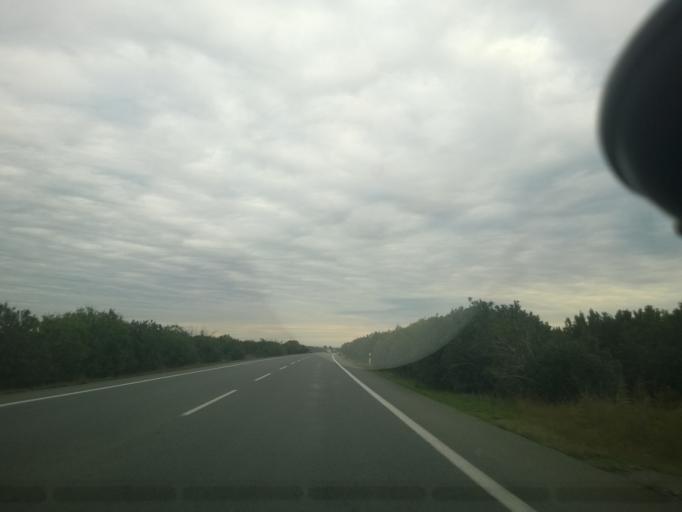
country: GR
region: Central Macedonia
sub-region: Nomos Pellis
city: Palaifyto
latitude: 40.8089
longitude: 22.2328
